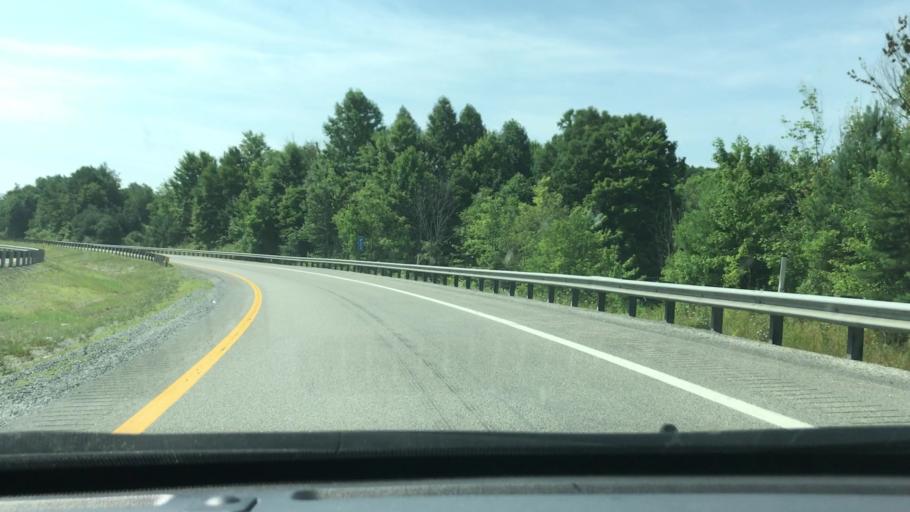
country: US
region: West Virginia
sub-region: Raleigh County
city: Prosperity
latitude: 37.8322
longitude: -81.2169
